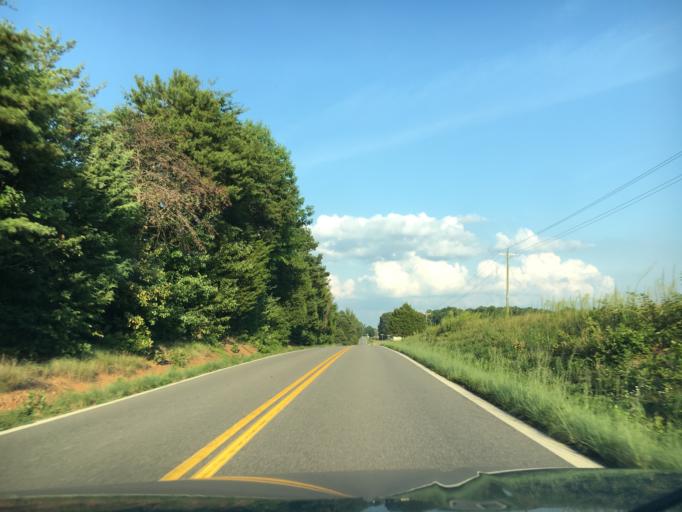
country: US
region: Virginia
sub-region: Halifax County
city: Mountain Road
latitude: 36.8320
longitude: -79.1197
